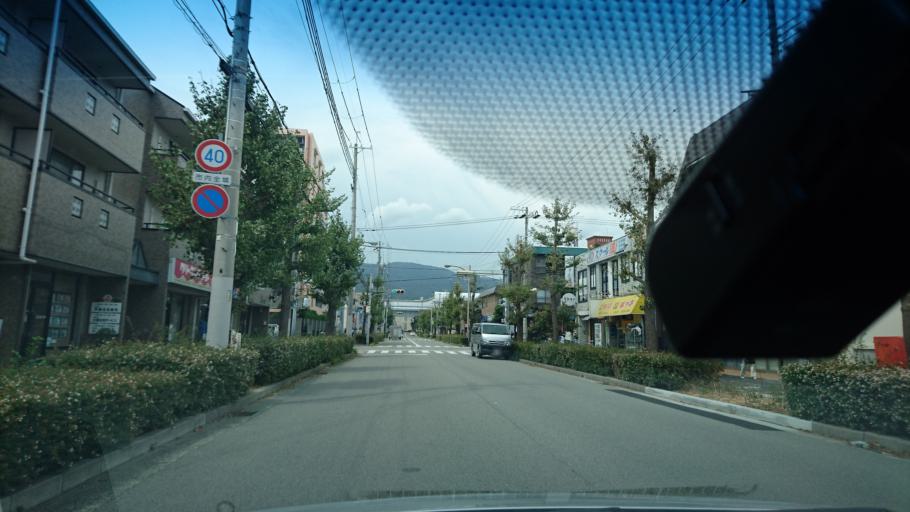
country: JP
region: Hyogo
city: Ashiya
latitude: 34.7287
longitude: 135.3181
